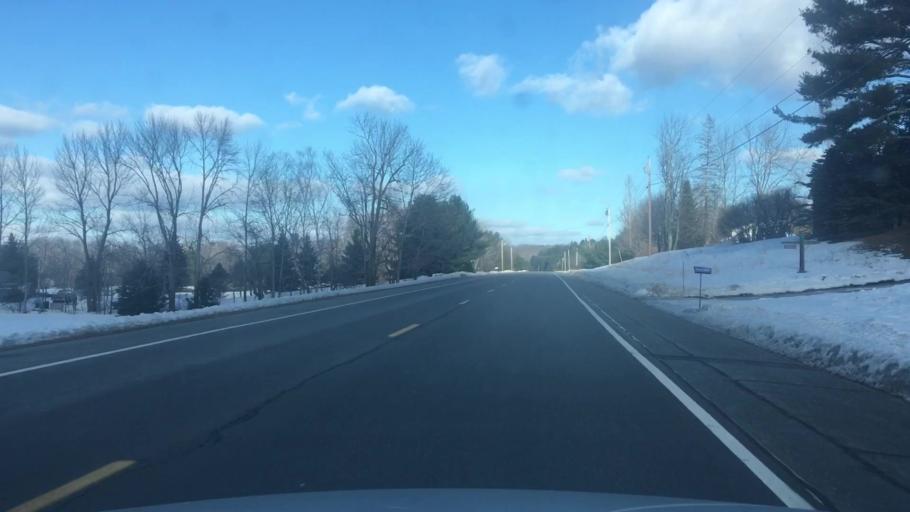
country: US
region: Maine
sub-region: Somerset County
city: Madison
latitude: 45.0191
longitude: -69.8576
